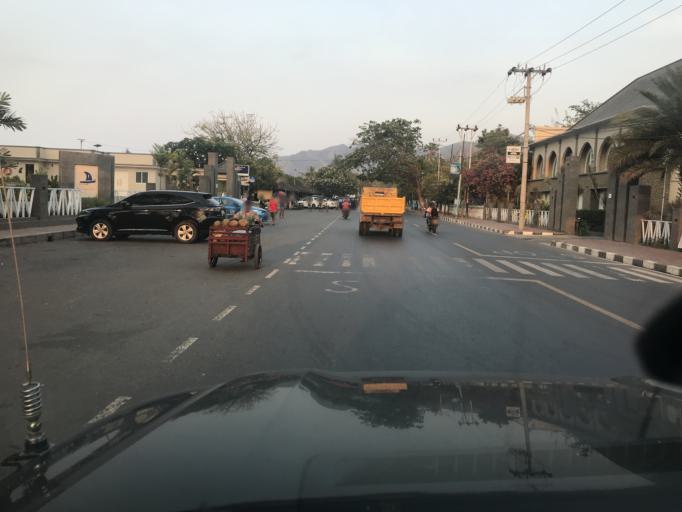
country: TL
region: Dili
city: Dili
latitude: -8.5487
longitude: 125.5865
